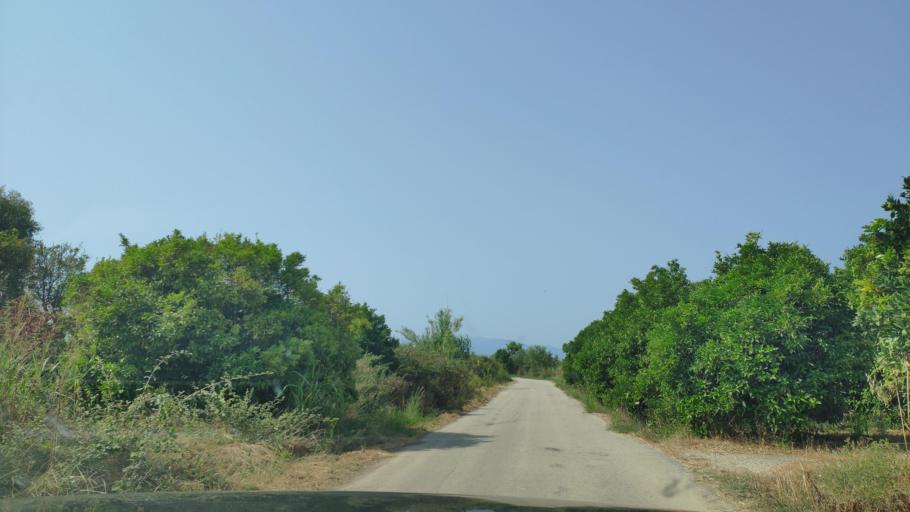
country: GR
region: Epirus
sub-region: Nomos Artas
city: Kompoti
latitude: 39.0595
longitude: 21.0729
